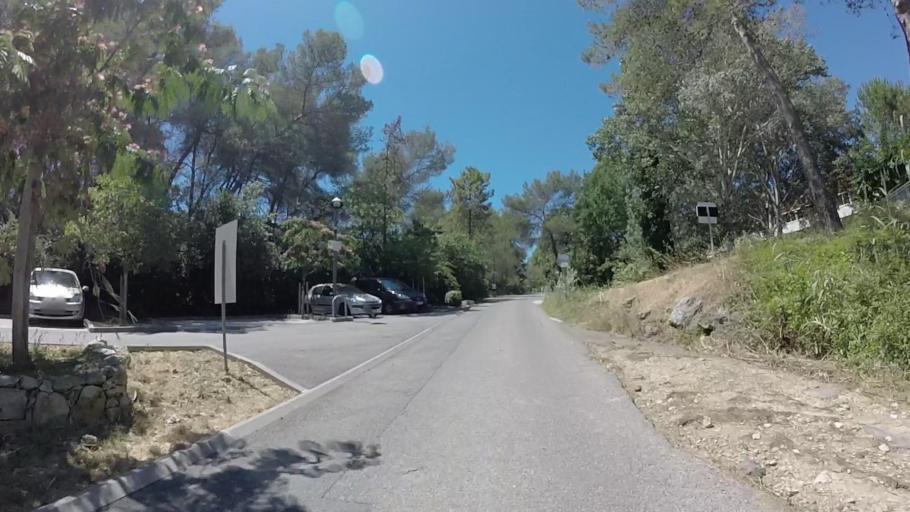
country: FR
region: Provence-Alpes-Cote d'Azur
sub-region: Departement des Alpes-Maritimes
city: Valbonne
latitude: 43.6258
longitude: 7.0388
